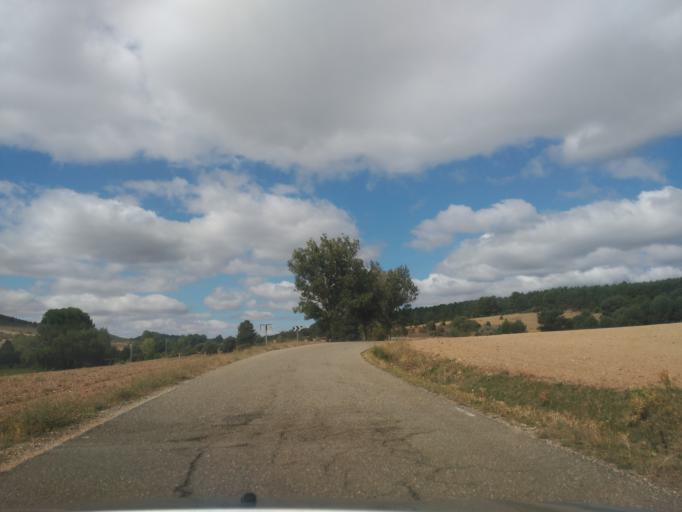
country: ES
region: Castille and Leon
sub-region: Provincia de Burgos
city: Rabanera del Pinar
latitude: 41.8547
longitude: -3.2056
